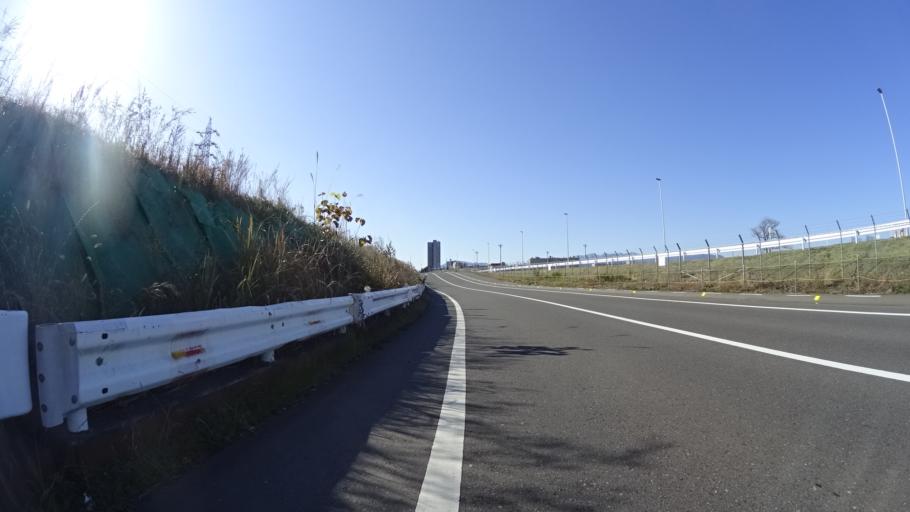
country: JP
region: Tokyo
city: Hachioji
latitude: 35.5878
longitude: 139.3772
